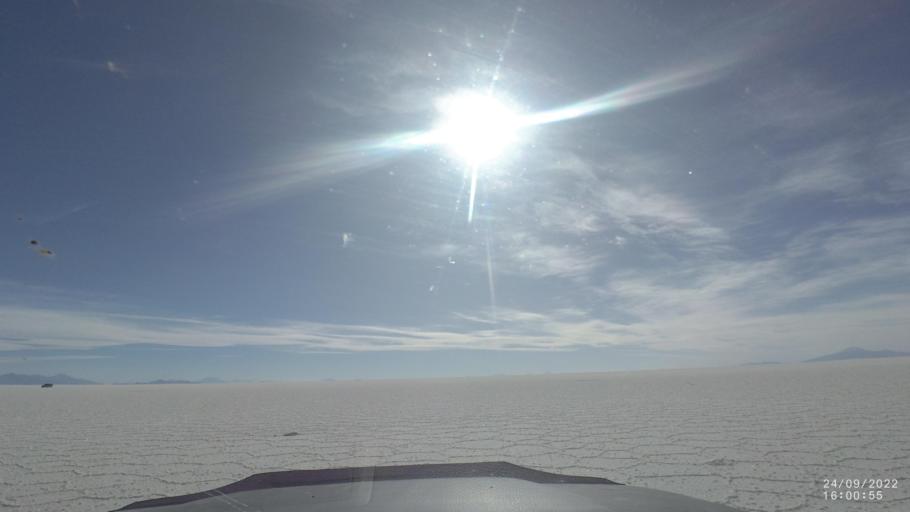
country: BO
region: Potosi
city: Colchani
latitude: -20.3223
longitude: -67.2535
